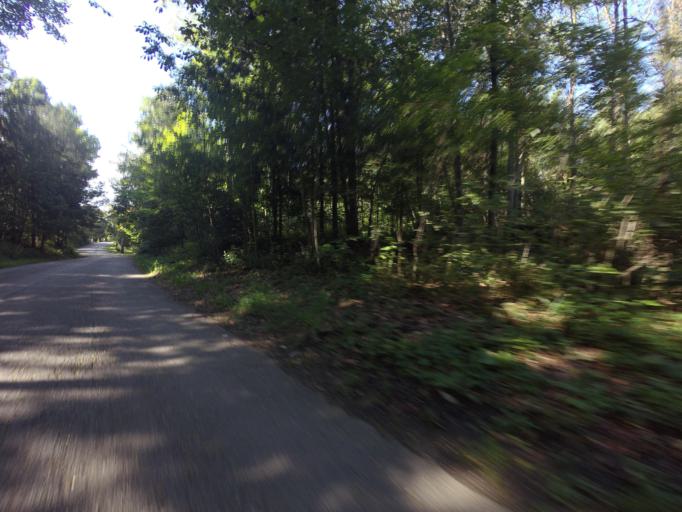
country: CA
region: Ontario
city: Waterloo
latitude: 43.6661
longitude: -80.4500
